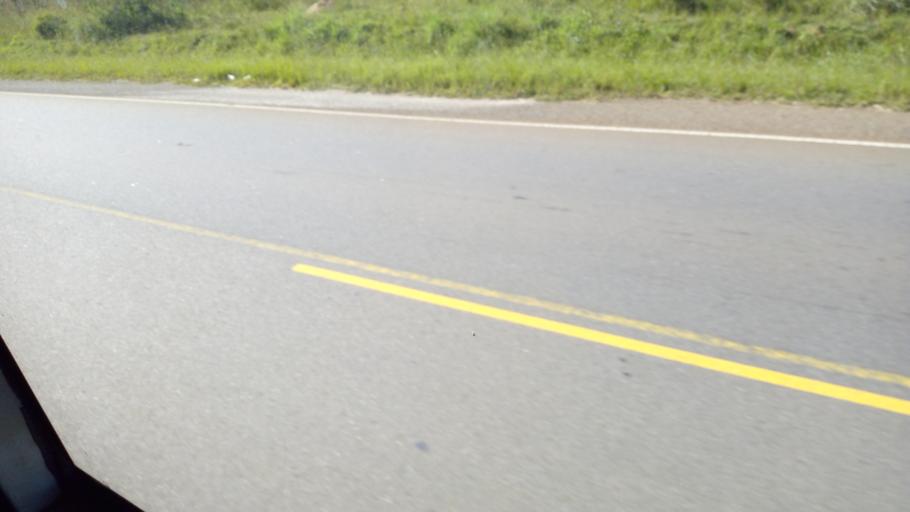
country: UG
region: Central Region
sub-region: Lyantonde District
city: Lyantonde
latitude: -0.4512
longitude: 31.0577
